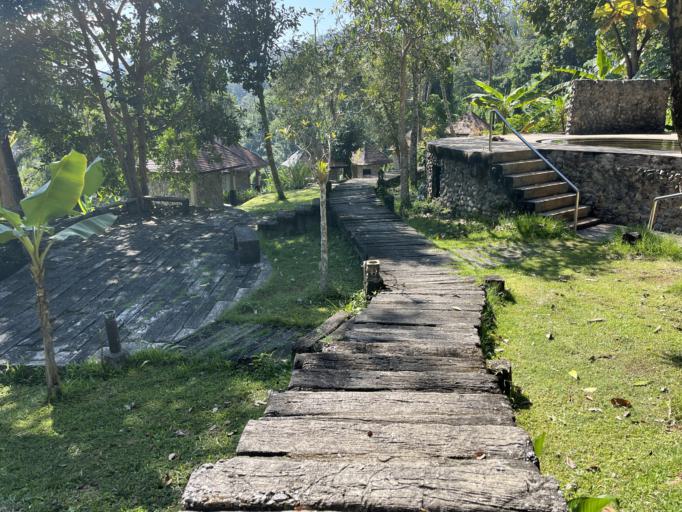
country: TH
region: Mae Hong Son
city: Mae Hi
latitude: 19.2439
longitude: 98.6887
